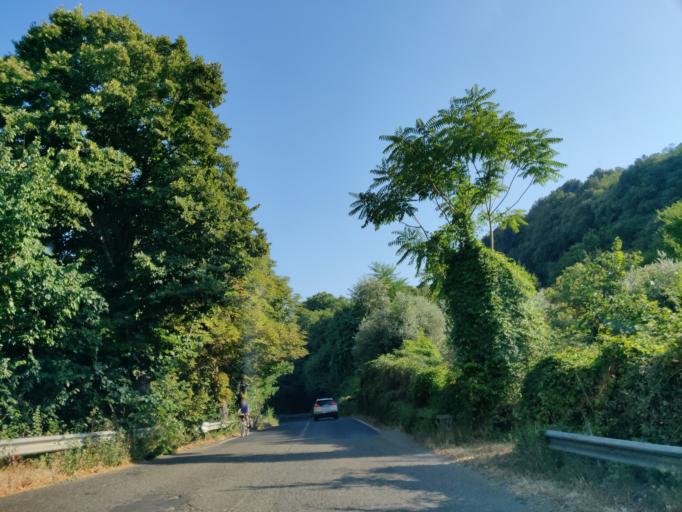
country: IT
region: Latium
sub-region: Provincia di Viterbo
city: Acquapendente
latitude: 42.7518
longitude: 11.8633
